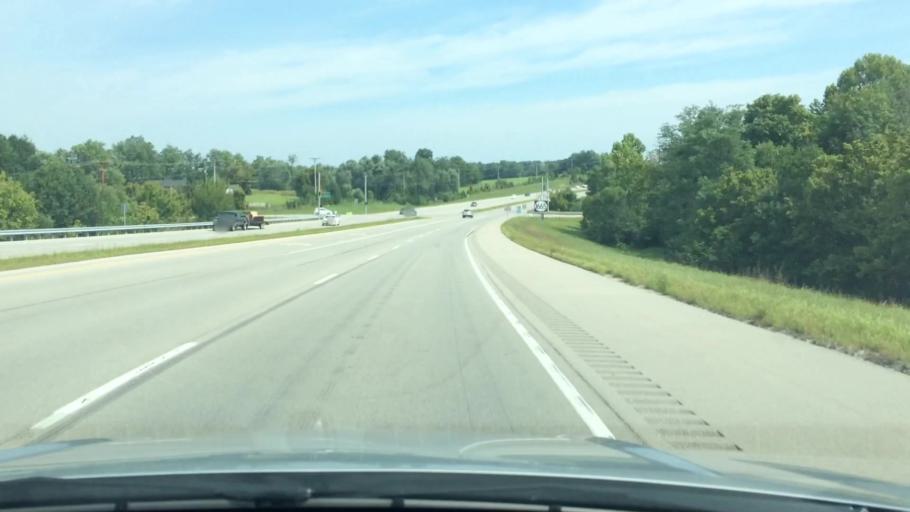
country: US
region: Kentucky
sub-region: Franklin County
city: Frankfort
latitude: 38.1293
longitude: -84.9130
